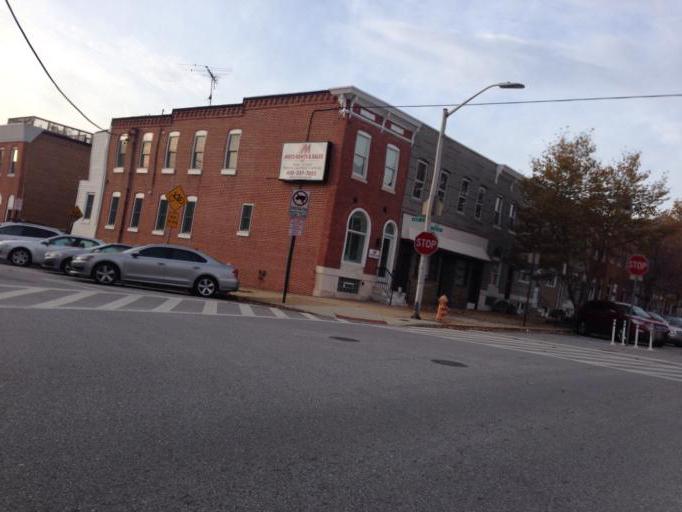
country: US
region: Maryland
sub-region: City of Baltimore
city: Baltimore
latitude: 39.2835
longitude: -76.5670
